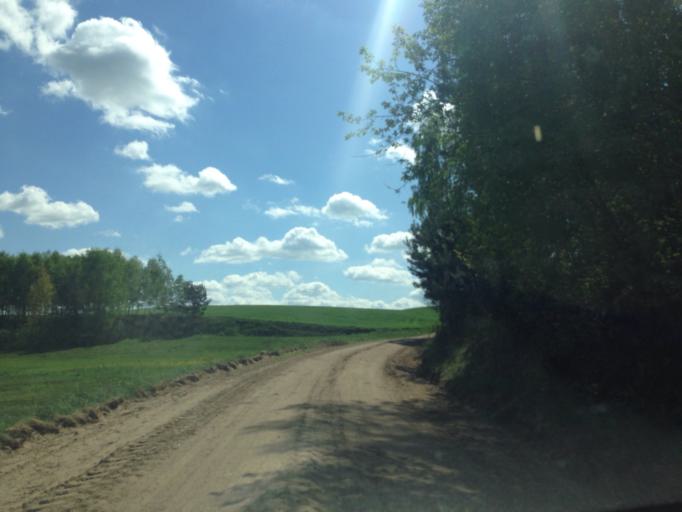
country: PL
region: Kujawsko-Pomorskie
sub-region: Powiat brodnicki
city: Brzozie
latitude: 53.3029
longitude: 19.6550
